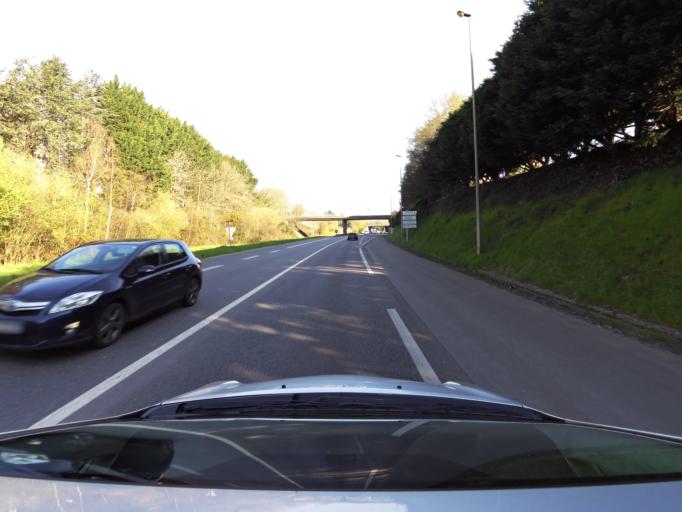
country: FR
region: Brittany
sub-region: Departement du Morbihan
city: Lorient
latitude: 47.7455
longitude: -3.3861
